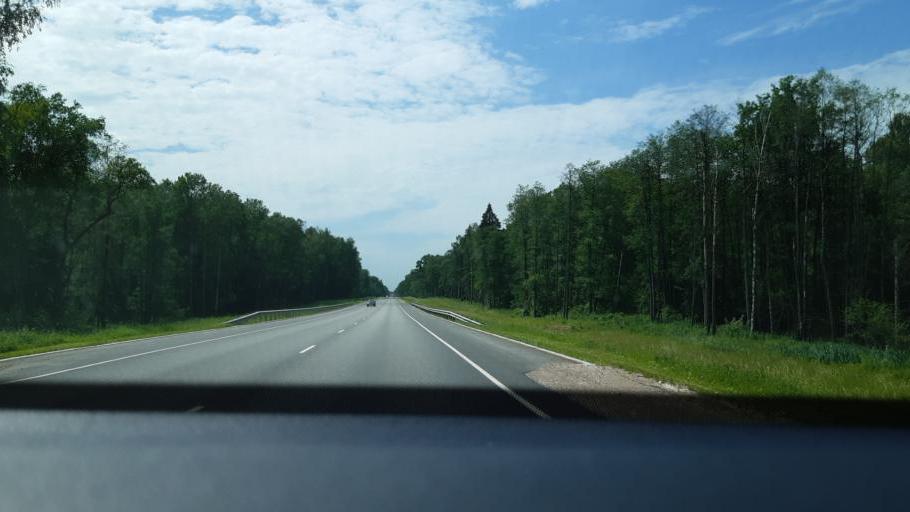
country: RU
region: Kaluga
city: Medyn'
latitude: 54.9675
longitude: 35.9452
